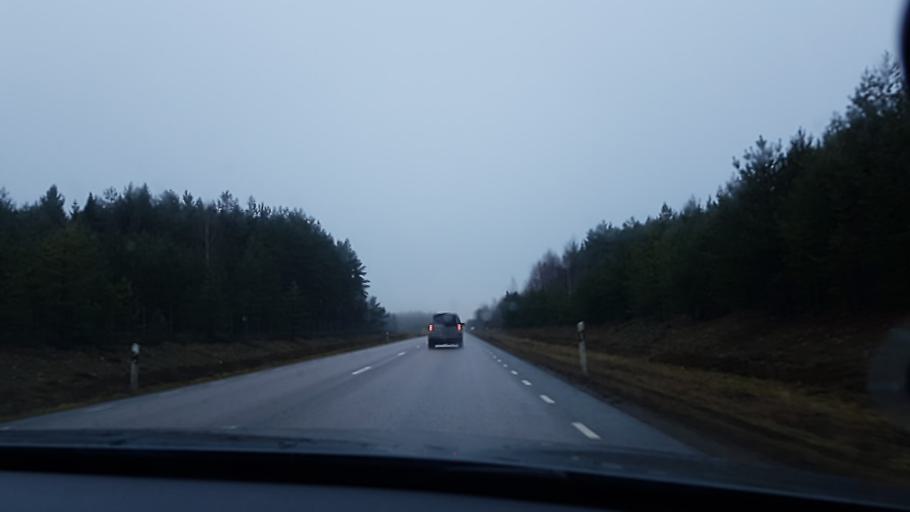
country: SE
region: Vaestra Goetaland
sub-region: Toreboda Kommun
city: Toereboda
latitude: 58.8120
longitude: 13.9796
